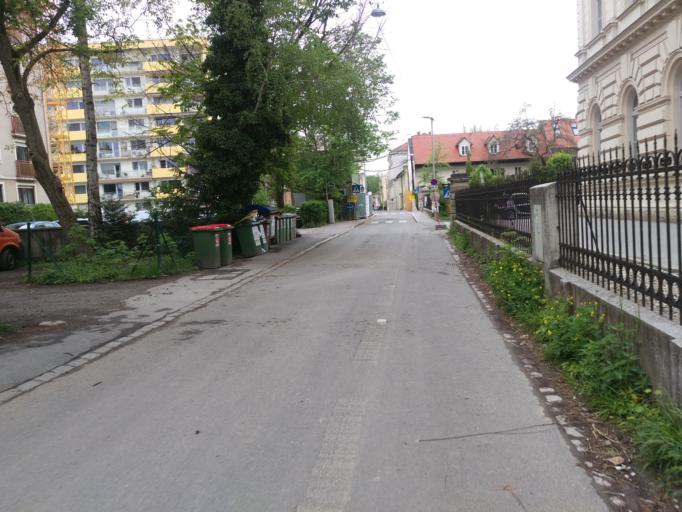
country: AT
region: Styria
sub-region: Graz Stadt
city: Graz
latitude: 47.0813
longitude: 15.4485
